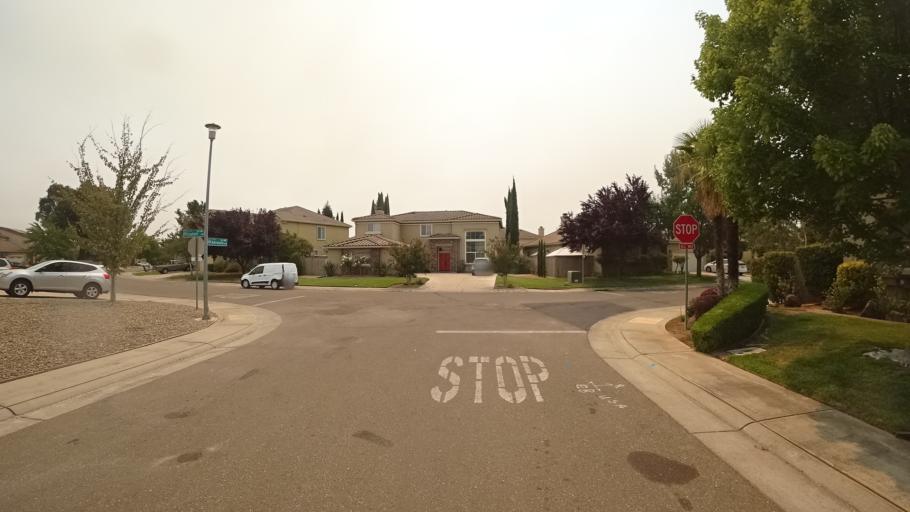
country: US
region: California
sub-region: Sacramento County
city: Laguna
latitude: 38.4005
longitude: -121.4205
